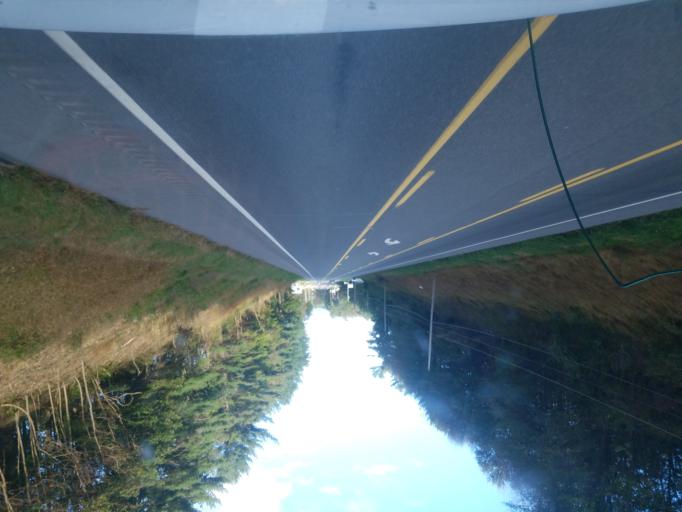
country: US
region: Pennsylvania
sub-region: Franklin County
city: Fayetteville
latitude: 39.8983
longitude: -77.4323
